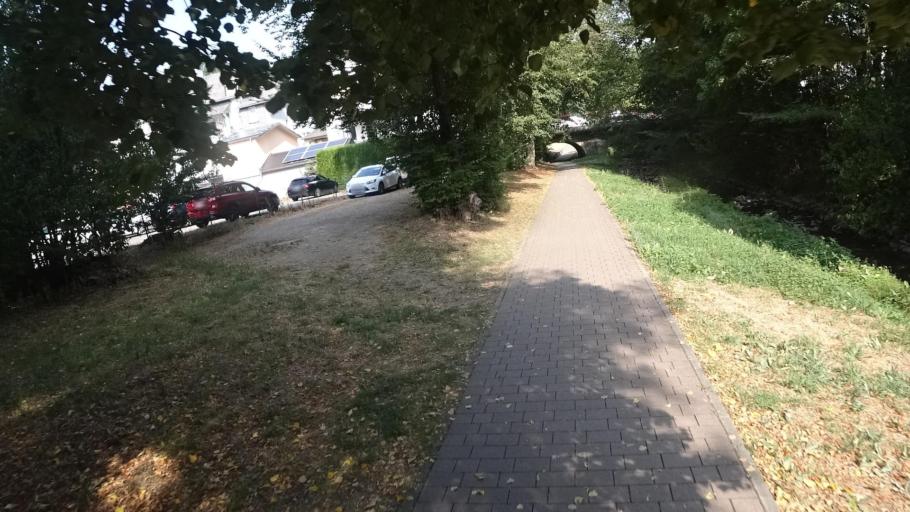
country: DE
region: Rheinland-Pfalz
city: Kumbdchen
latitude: 49.9823
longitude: 7.5191
